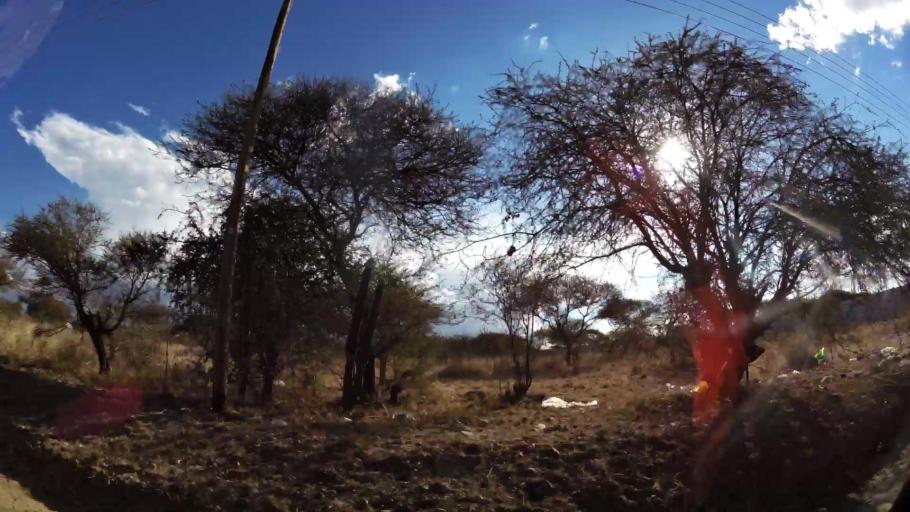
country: ZA
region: Limpopo
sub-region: Capricorn District Municipality
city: Polokwane
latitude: -23.9362
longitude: 29.4444
